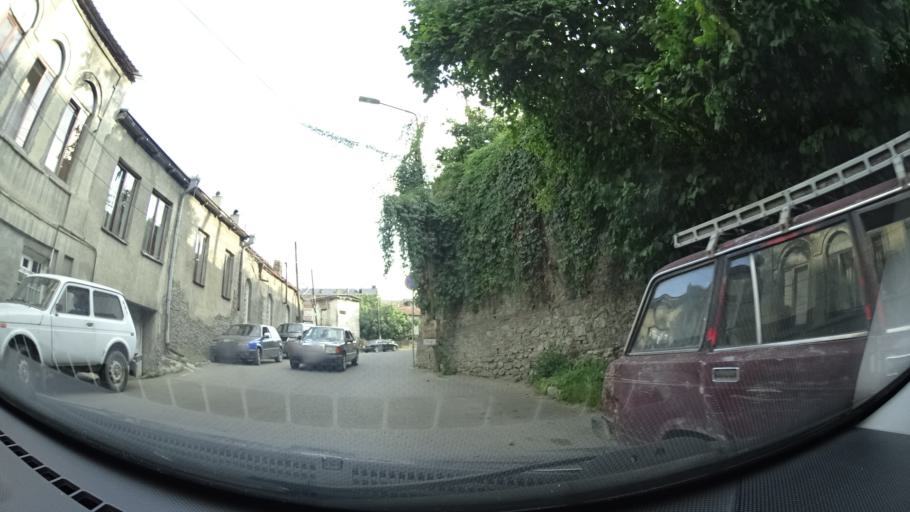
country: GE
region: Kakheti
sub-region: Telavi
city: Telavi
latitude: 41.9203
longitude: 45.4727
